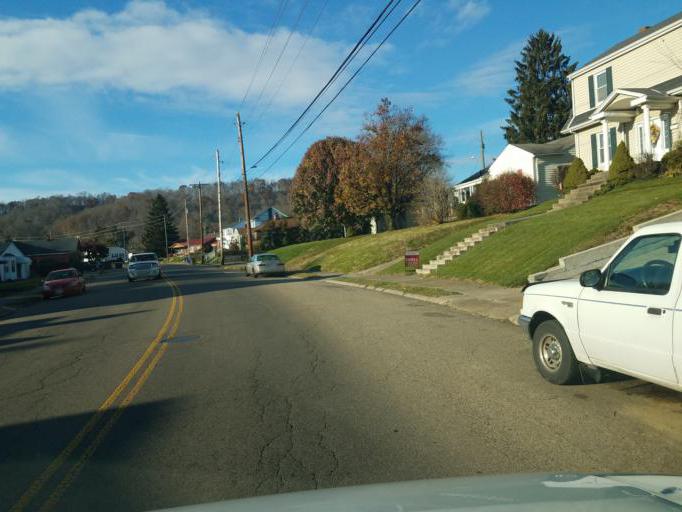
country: US
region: Ohio
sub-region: Scioto County
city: Rosemount
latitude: 38.7576
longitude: -82.9768
